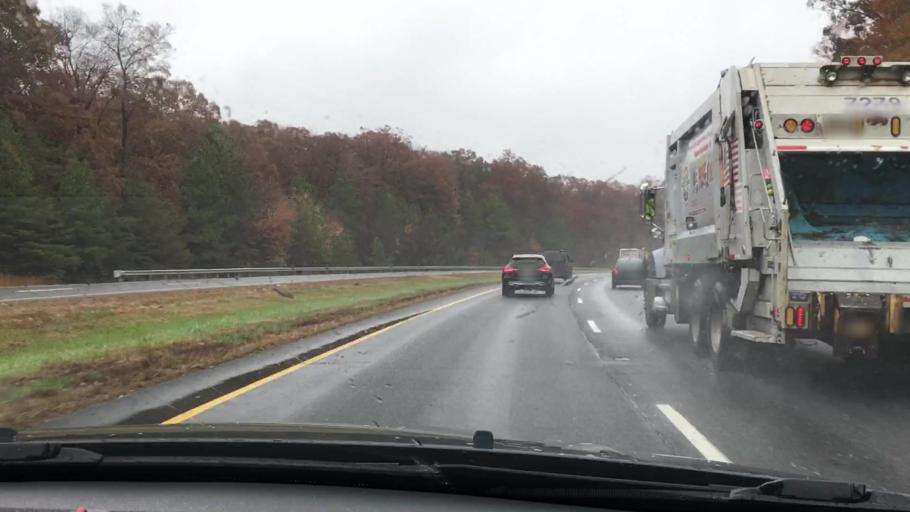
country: US
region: Virginia
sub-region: Fairfax County
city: Fairfax Station
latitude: 38.8228
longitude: -77.3532
